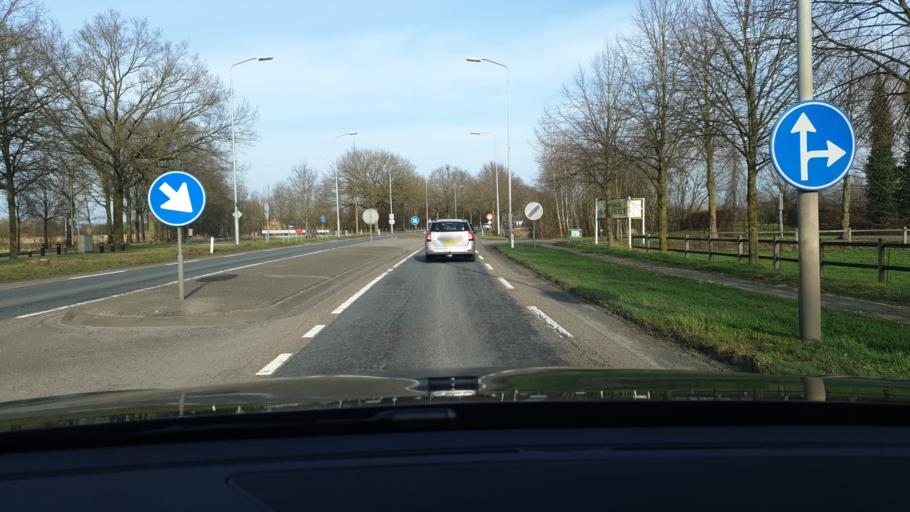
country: NL
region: North Brabant
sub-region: Gemeente Oirschot
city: Oostelbeers
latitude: 51.4903
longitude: 5.2884
